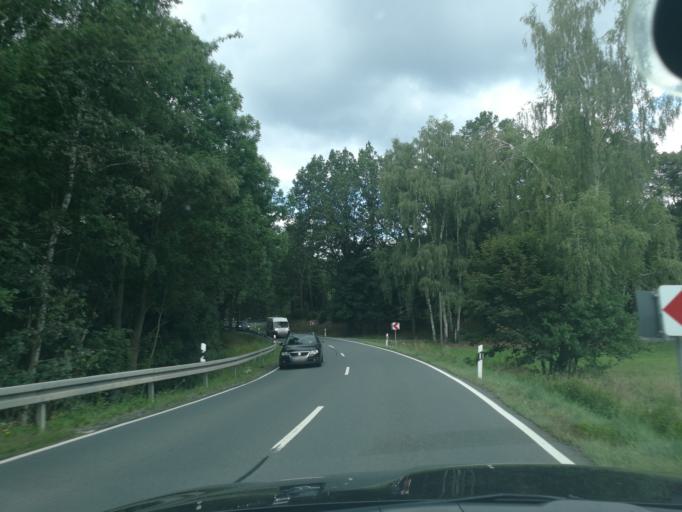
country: DE
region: Saxony
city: Oelsnitz
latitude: 50.3856
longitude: 12.1964
